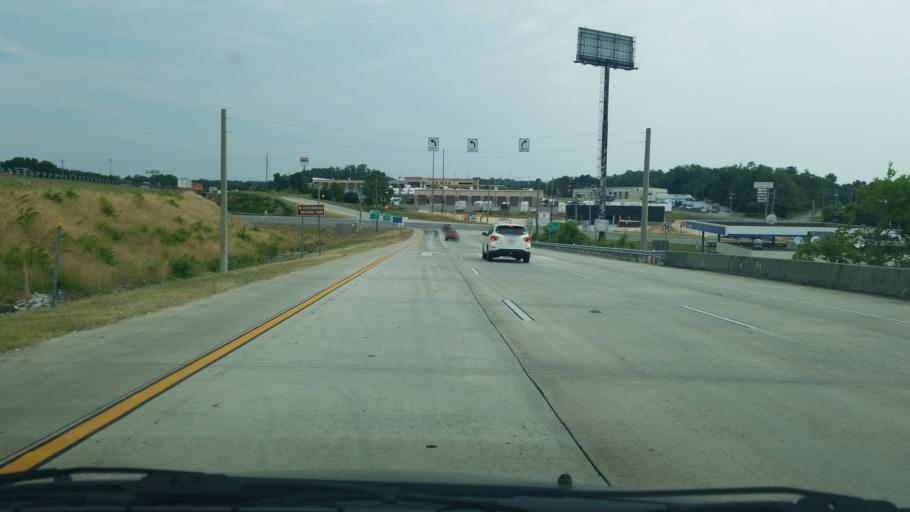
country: US
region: Georgia
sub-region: Catoosa County
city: Indian Springs
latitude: 34.9265
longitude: -85.1511
